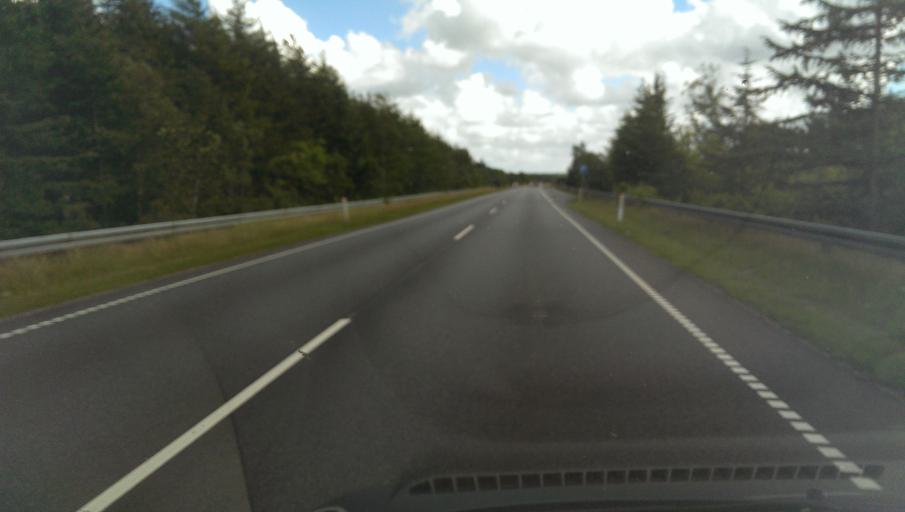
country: DK
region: South Denmark
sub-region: Varde Kommune
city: Varde
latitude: 55.6504
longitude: 8.5088
